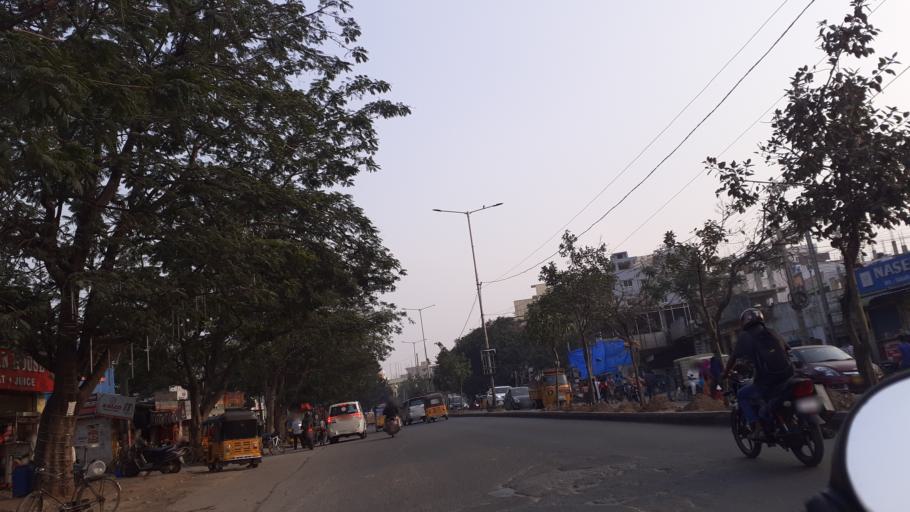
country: IN
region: Telangana
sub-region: Rangareddi
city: Kukatpalli
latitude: 17.4783
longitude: 78.3620
